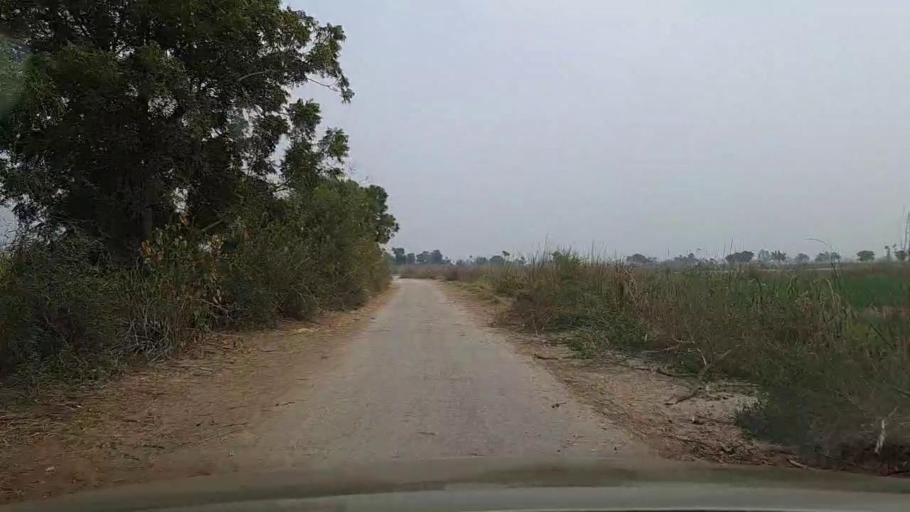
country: PK
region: Sindh
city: Sanghar
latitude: 26.1392
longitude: 68.9339
